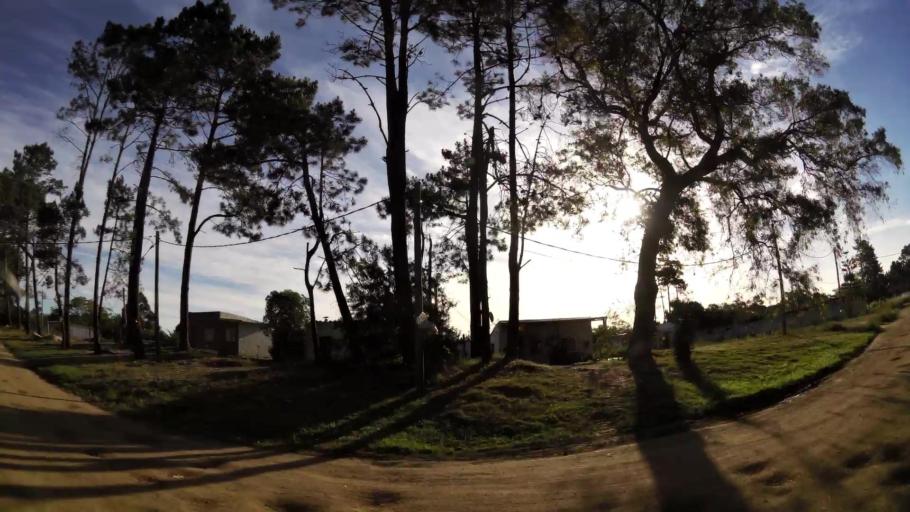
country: UY
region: Canelones
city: Empalme Olmos
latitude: -34.7736
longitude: -55.8591
